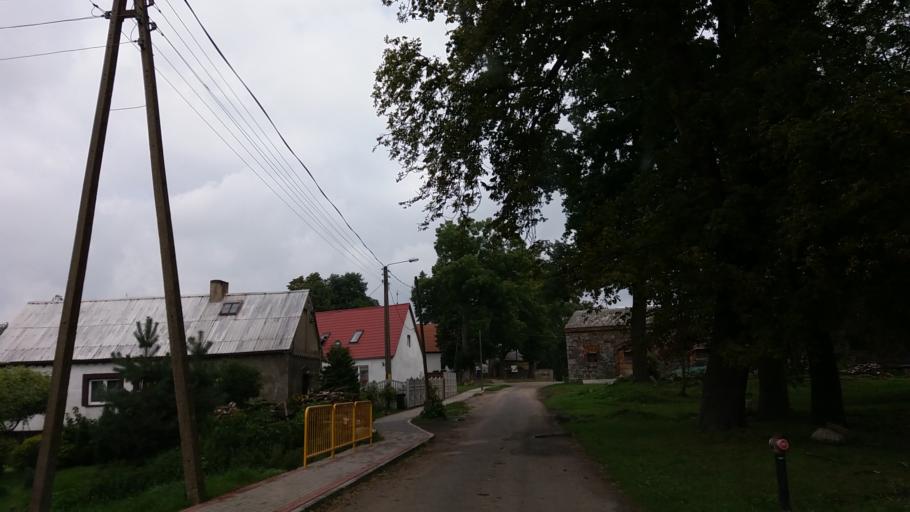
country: PL
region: West Pomeranian Voivodeship
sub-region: Powiat choszczenski
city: Krzecin
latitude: 53.1131
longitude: 15.4927
